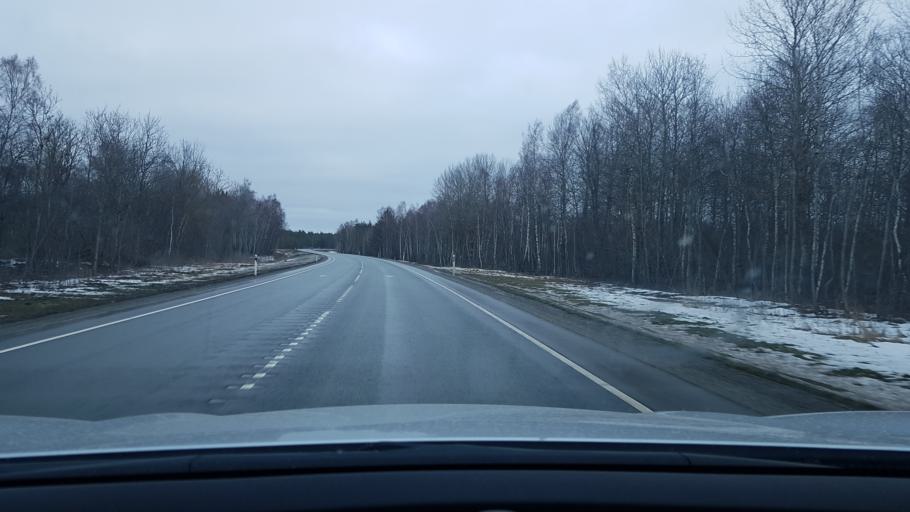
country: EE
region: Laeaene
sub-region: Lihula vald
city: Lihula
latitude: 58.5991
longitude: 23.5517
